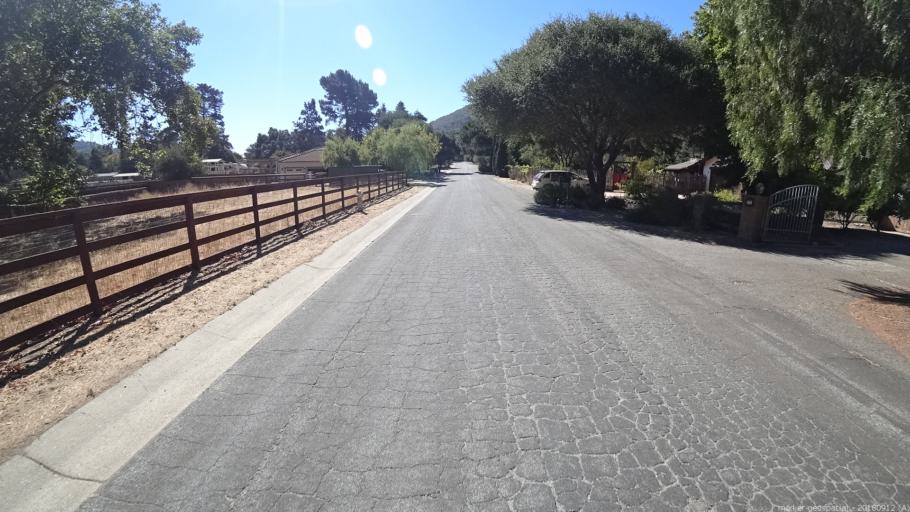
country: US
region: California
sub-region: Monterey County
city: Carmel Valley Village
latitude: 36.4946
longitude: -121.7568
